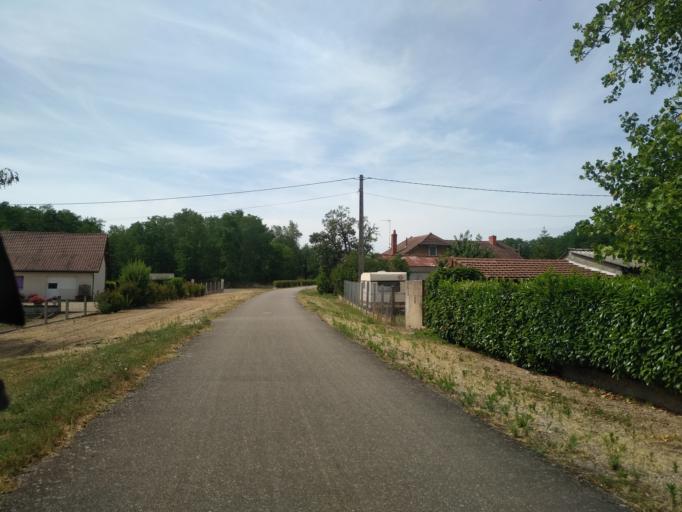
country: FR
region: Auvergne
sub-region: Departement de l'Allier
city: Diou
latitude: 46.5398
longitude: 3.7509
